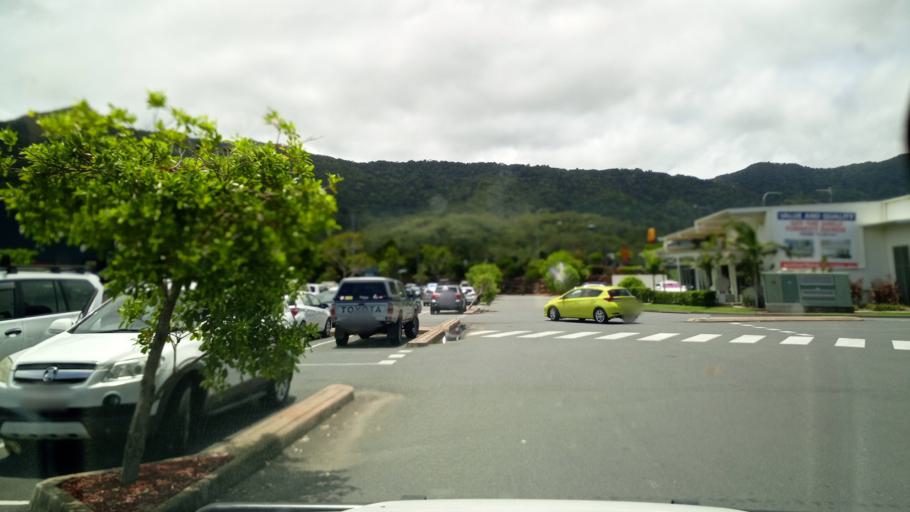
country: AU
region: Queensland
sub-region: Cairns
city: Redlynch
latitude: -16.8403
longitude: 145.6952
